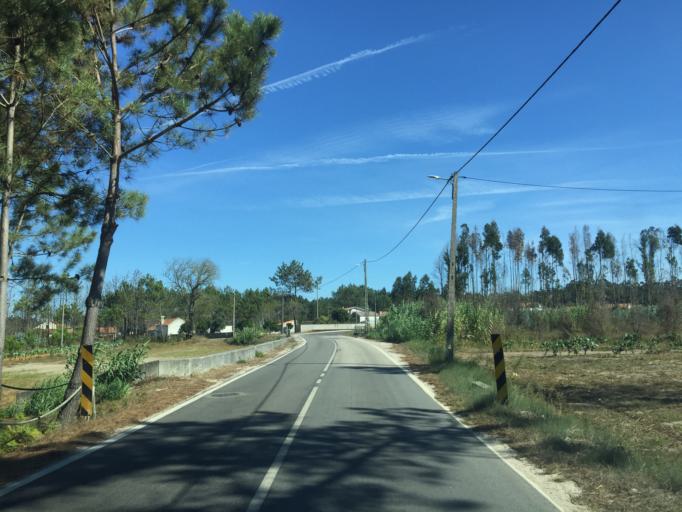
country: PT
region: Coimbra
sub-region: Figueira da Foz
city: Alhadas
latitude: 40.2218
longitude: -8.8236
